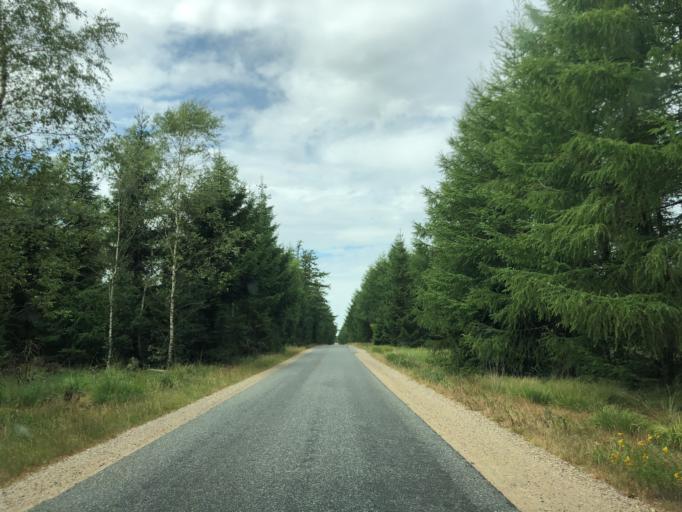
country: DK
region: South Denmark
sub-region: Billund Kommune
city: Grindsted
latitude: 55.6471
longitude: 8.9043
